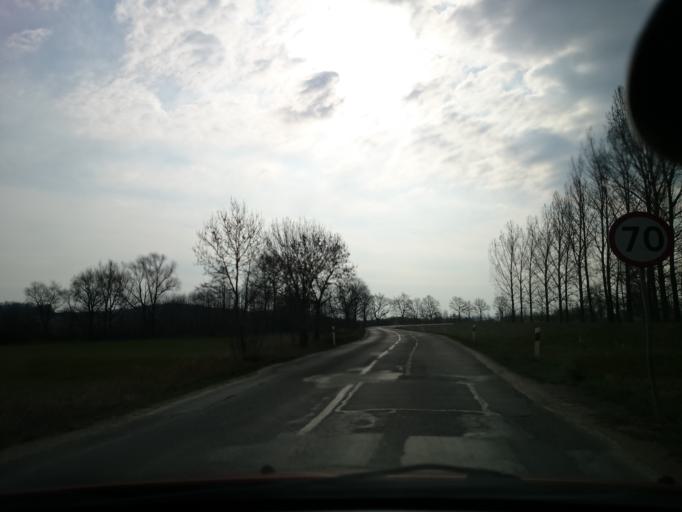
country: PL
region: Lower Silesian Voivodeship
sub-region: Powiat zabkowicki
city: Kamieniec Zabkowicki
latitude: 50.5108
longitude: 16.9295
